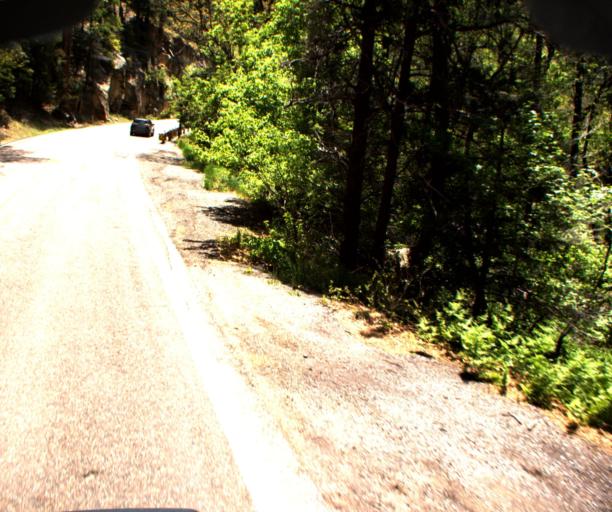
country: US
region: Arizona
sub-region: Coconino County
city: Kachina Village
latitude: 34.9920
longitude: -111.7358
